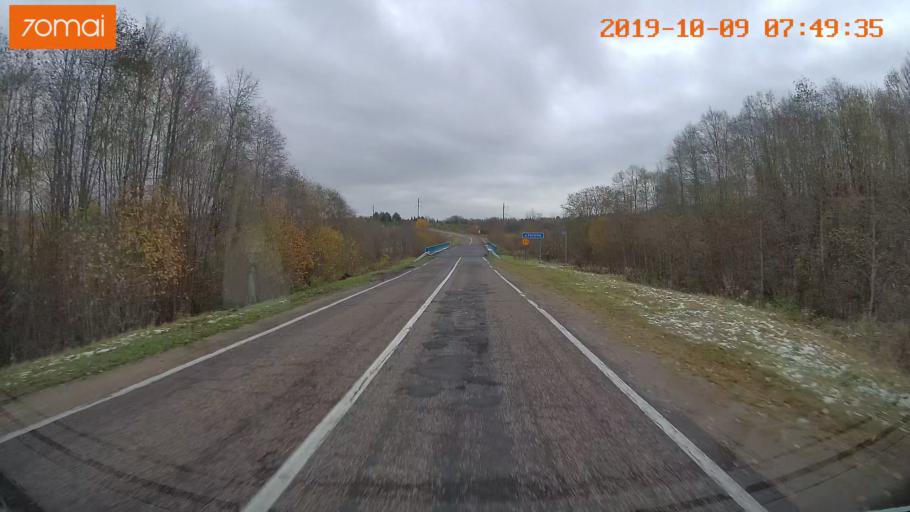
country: RU
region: Jaroslavl
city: Kukoboy
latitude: 58.6676
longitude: 39.8501
